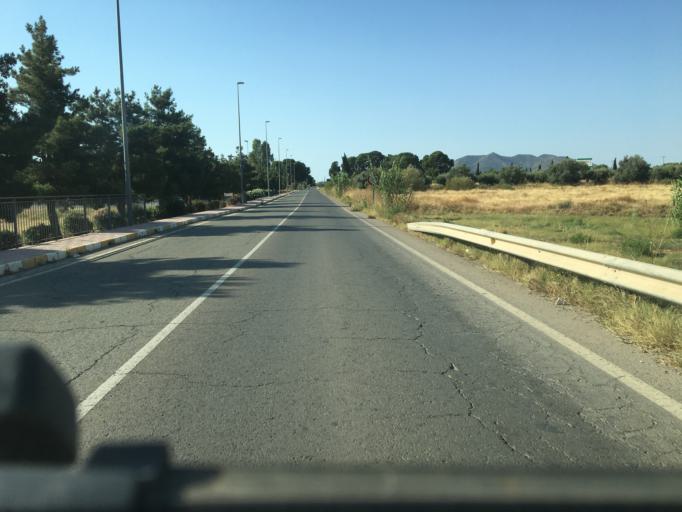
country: ES
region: Murcia
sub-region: Murcia
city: Puerto Lumbreras
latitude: 37.5482
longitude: -1.8153
